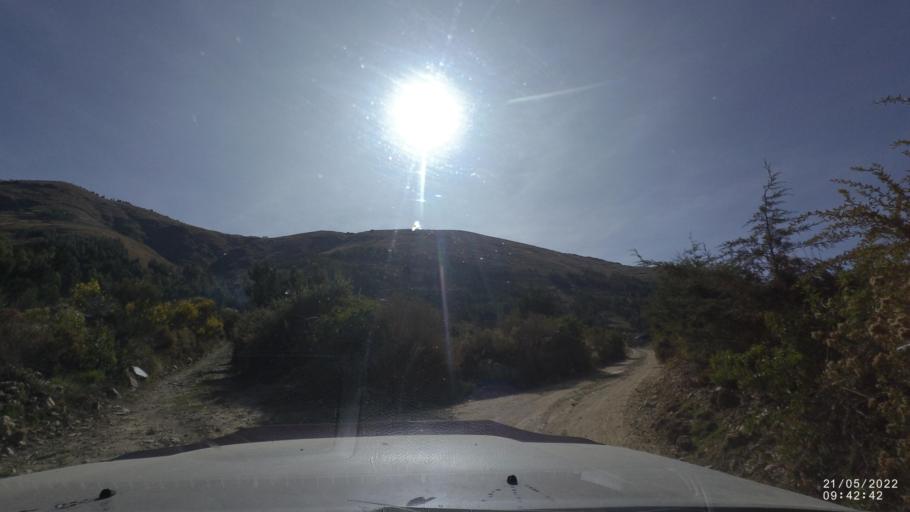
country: BO
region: Cochabamba
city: Colomi
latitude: -17.3407
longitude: -66.0104
